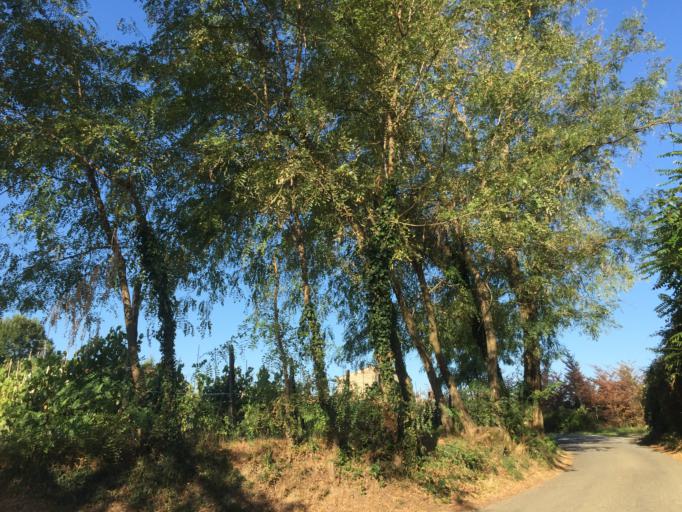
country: IT
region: Tuscany
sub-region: Provincia di Pistoia
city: Pistoia
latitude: 43.9480
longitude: 10.9455
